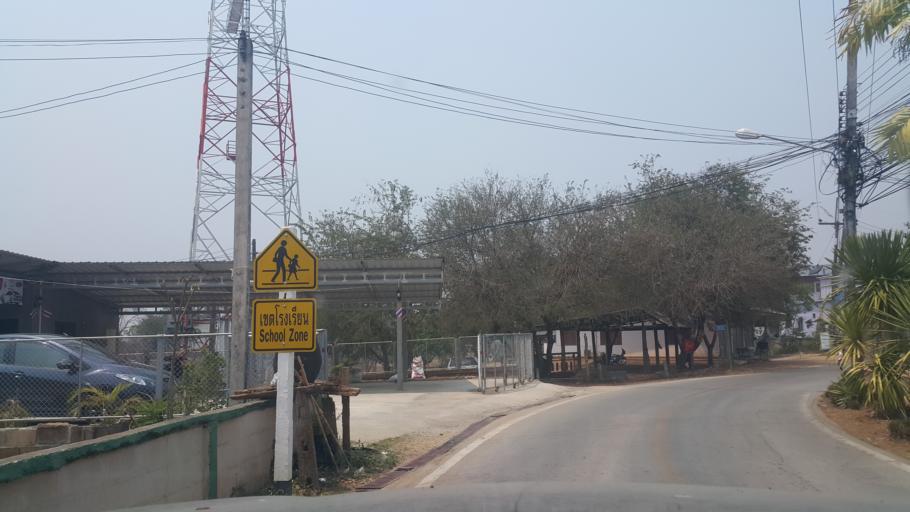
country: TH
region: Lampang
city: Soem Ngam
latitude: 18.0637
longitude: 99.2453
